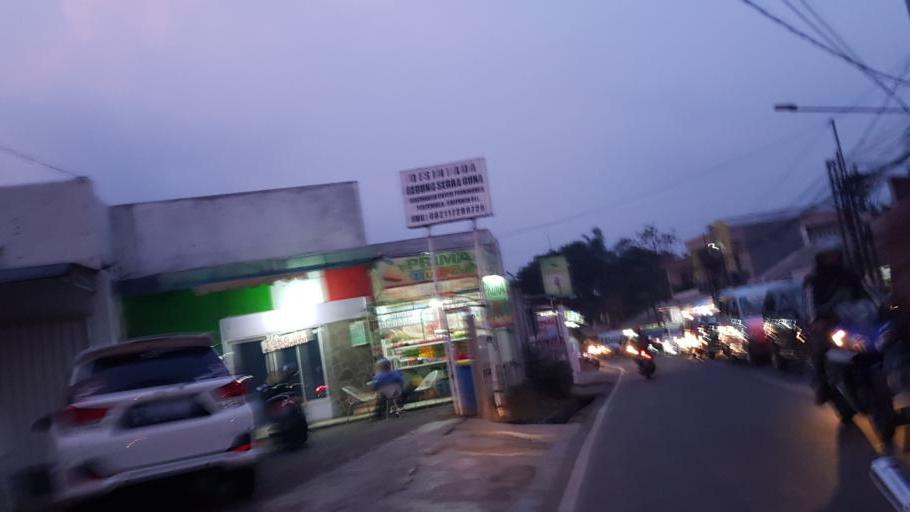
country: ID
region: West Java
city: Depok
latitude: -6.3480
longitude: 106.8021
